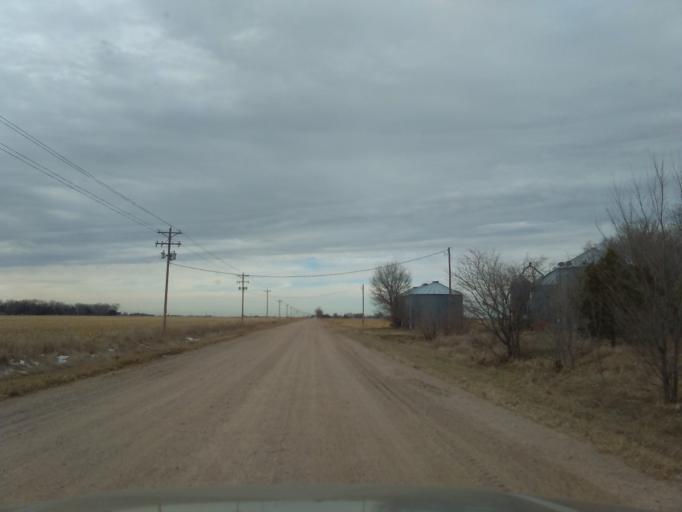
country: US
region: Nebraska
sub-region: Buffalo County
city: Gibbon
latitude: 40.6478
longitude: -98.8595
